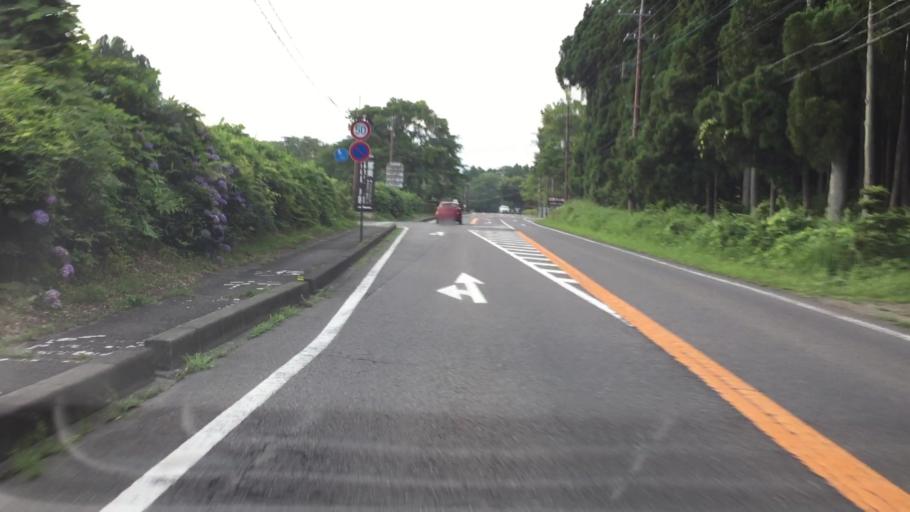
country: JP
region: Tochigi
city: Kuroiso
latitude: 37.0156
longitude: 140.0306
